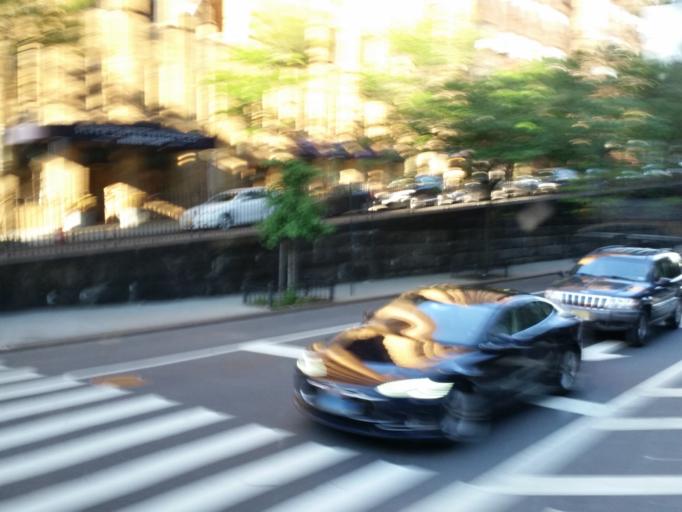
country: US
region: New York
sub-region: Queens County
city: Long Island City
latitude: 40.7532
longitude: -73.9666
